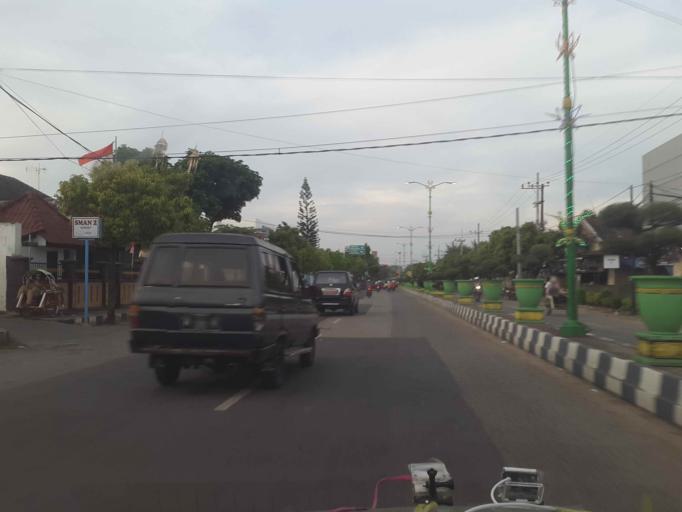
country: ID
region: East Java
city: Sumenep
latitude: -7.0158
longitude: 113.8581
